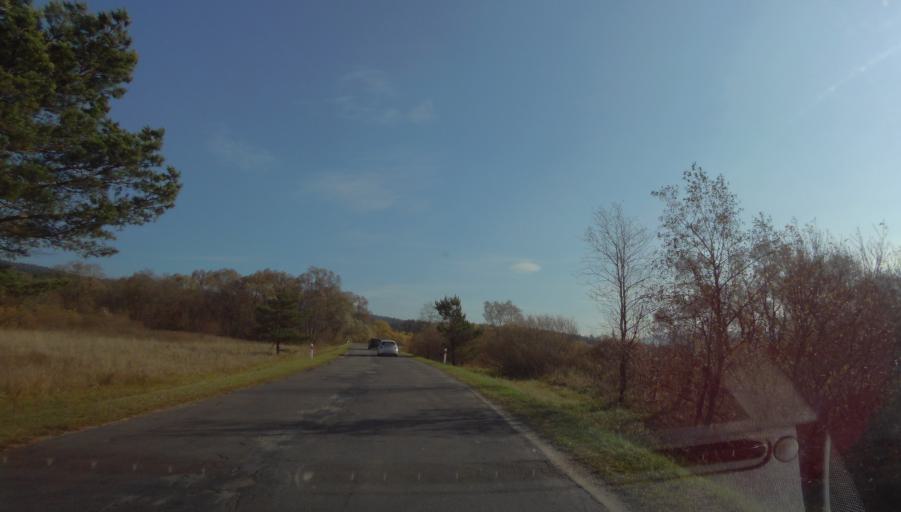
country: PL
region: Subcarpathian Voivodeship
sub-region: Powiat sanocki
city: Komancza
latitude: 49.2422
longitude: 22.1361
